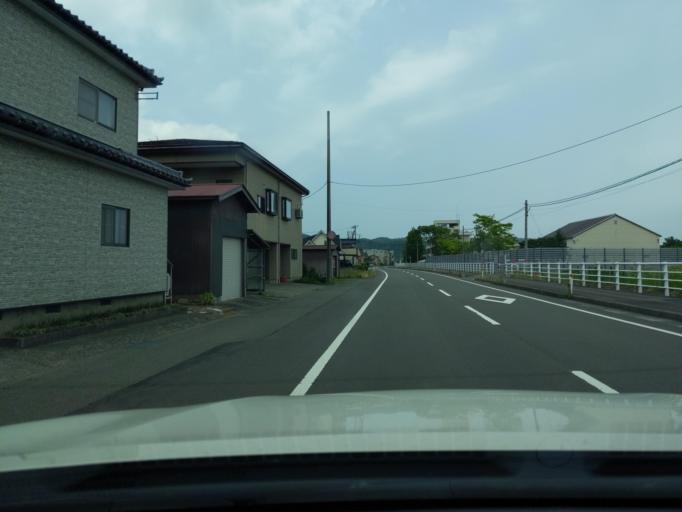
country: JP
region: Niigata
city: Kashiwazaki
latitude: 37.3302
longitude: 138.5686
